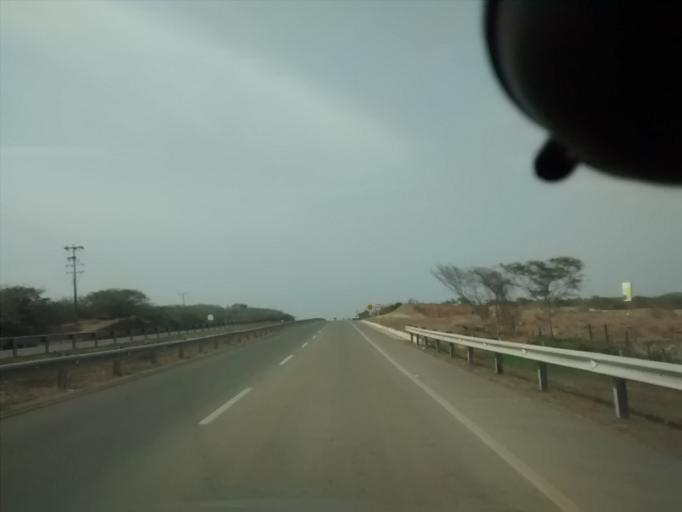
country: CO
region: Bolivar
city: Cartagena
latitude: 10.5070
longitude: -75.4725
